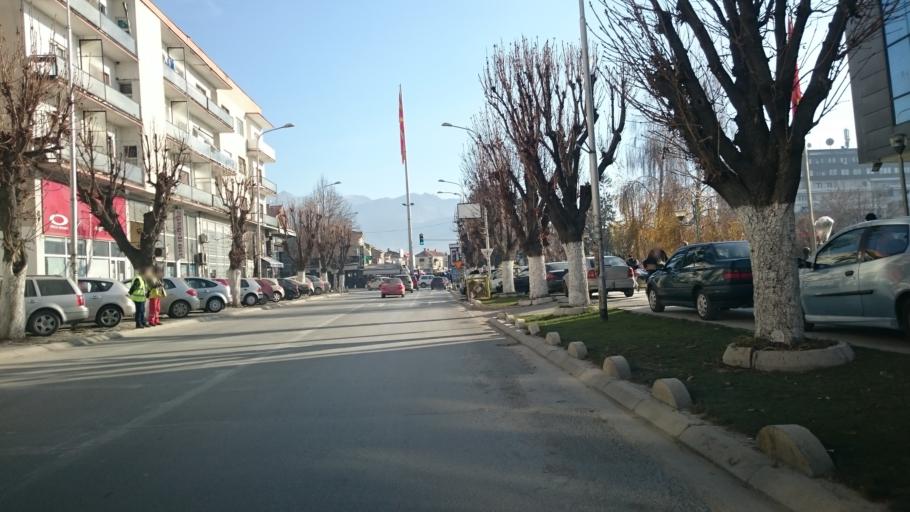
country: MK
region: Prilep
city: Prilep
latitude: 41.3469
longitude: 21.5530
